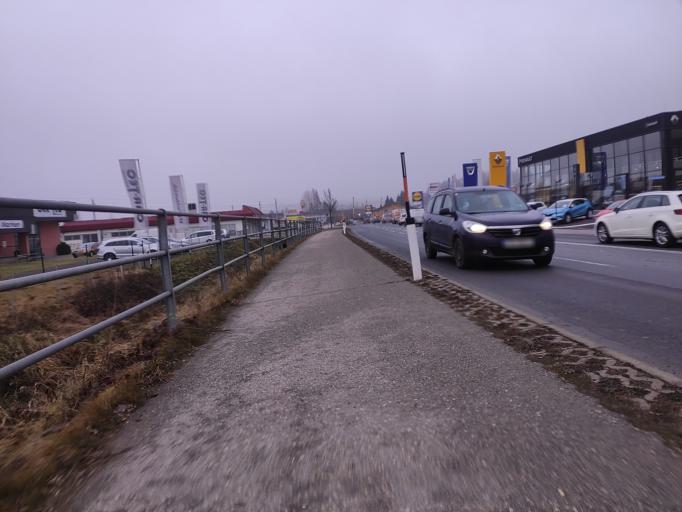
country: AT
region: Salzburg
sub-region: Politischer Bezirk Salzburg-Umgebung
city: Strasswalchen
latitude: 47.9716
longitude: 13.2497
